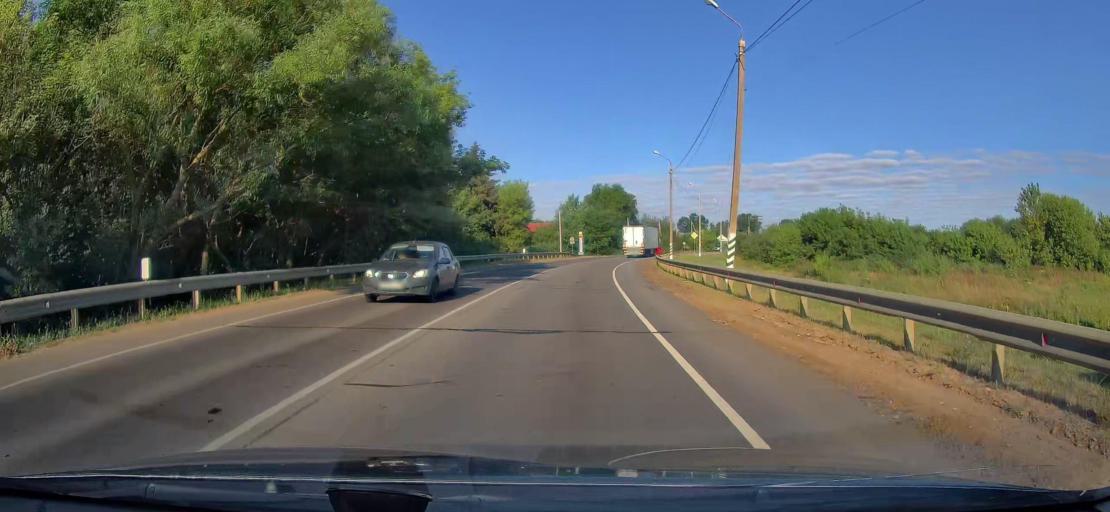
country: RU
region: Tula
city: Chern'
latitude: 53.4510
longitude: 36.8899
